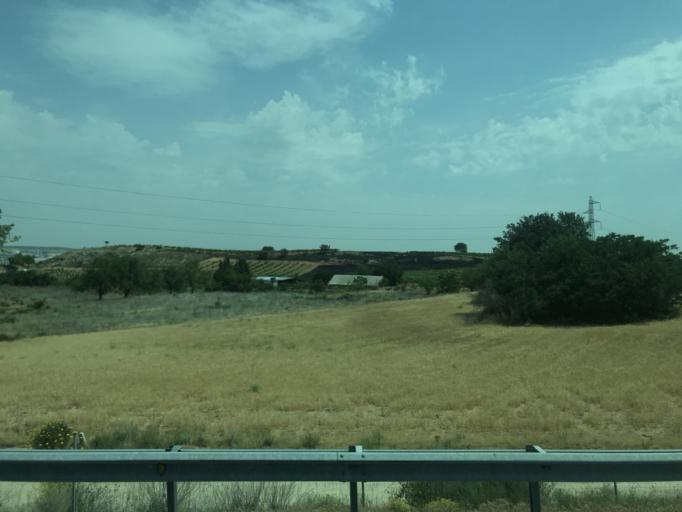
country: ES
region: Castille and Leon
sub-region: Provincia de Burgos
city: Fuentespina
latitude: 41.6451
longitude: -3.7145
